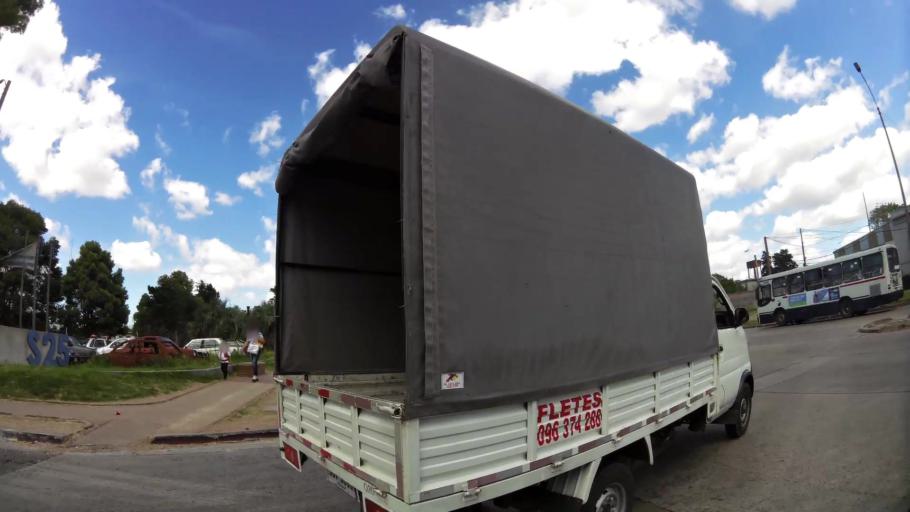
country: UY
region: Canelones
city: Paso de Carrasco
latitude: -34.8370
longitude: -56.1163
